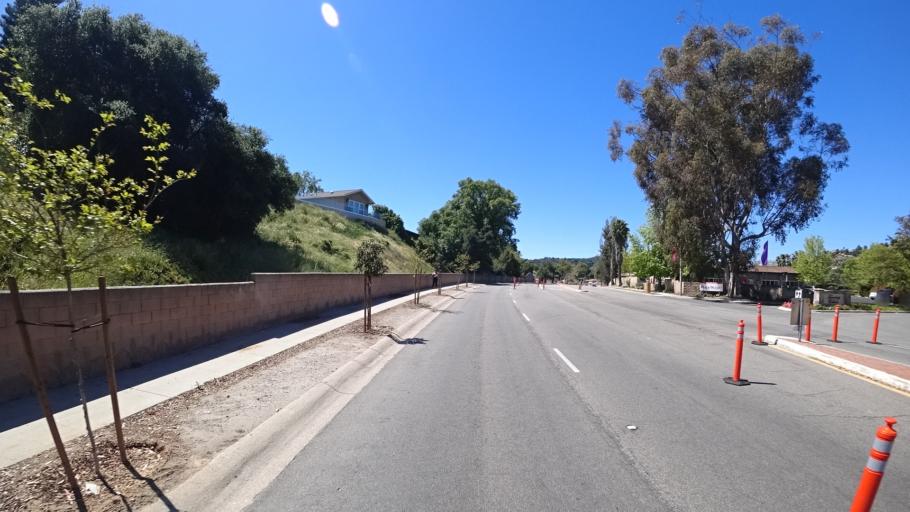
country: US
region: California
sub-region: Ventura County
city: Casa Conejo
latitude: 34.1767
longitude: -118.9523
